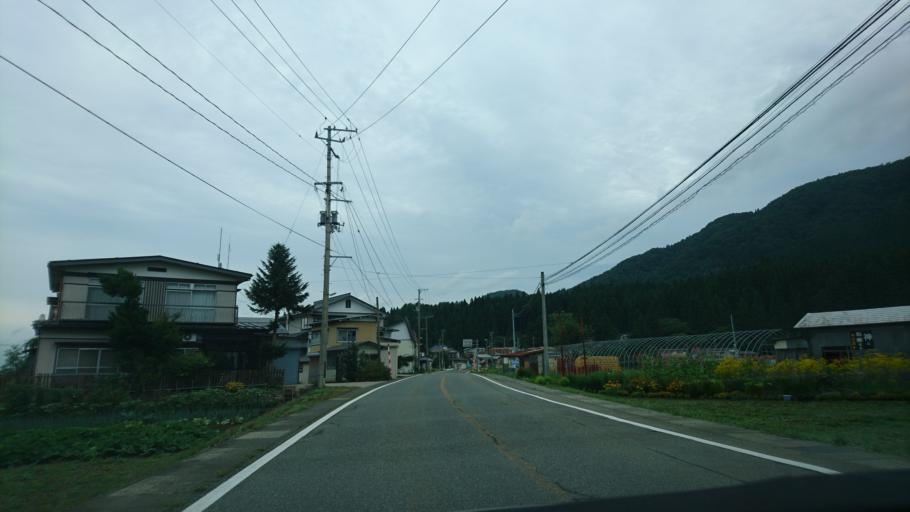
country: JP
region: Akita
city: Yuzawa
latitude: 39.1368
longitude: 140.5756
